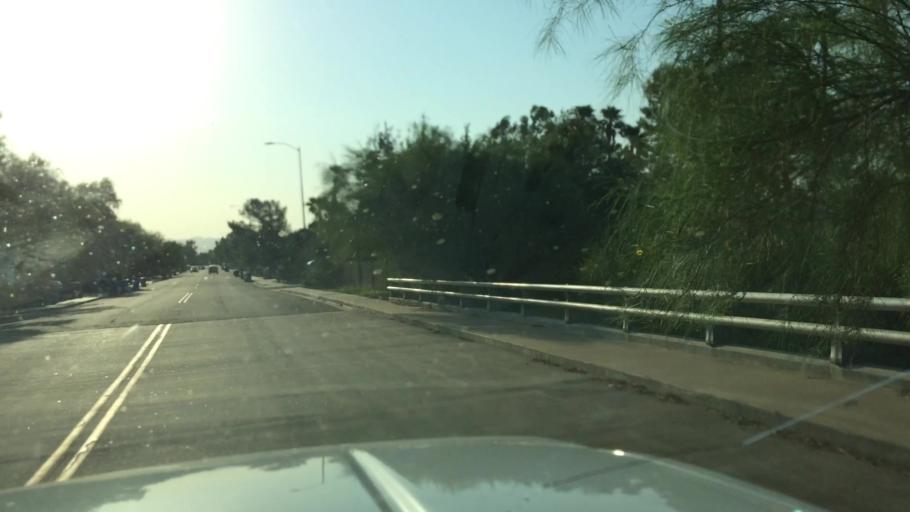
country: US
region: Arizona
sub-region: Maricopa County
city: Paradise Valley
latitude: 33.6187
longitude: -111.9475
